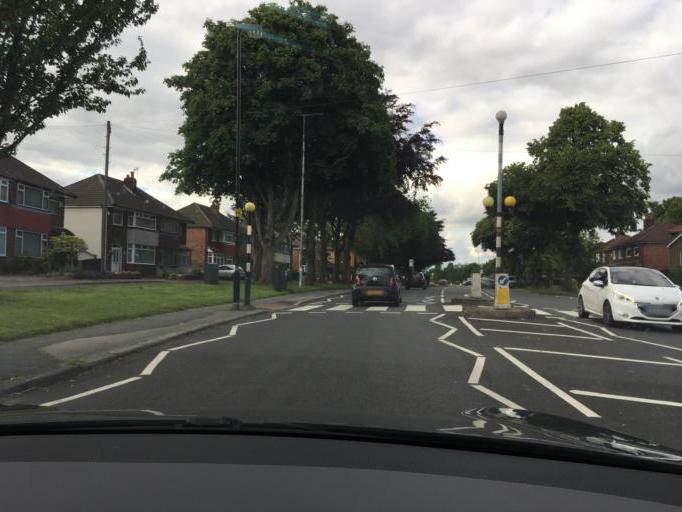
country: GB
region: England
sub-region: Trafford
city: Urmston
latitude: 53.4601
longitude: -2.3582
